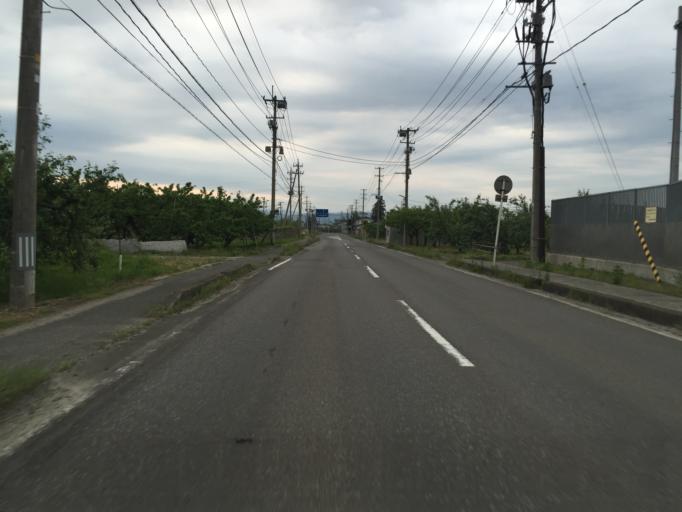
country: JP
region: Fukushima
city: Fukushima-shi
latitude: 37.8152
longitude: 140.4601
